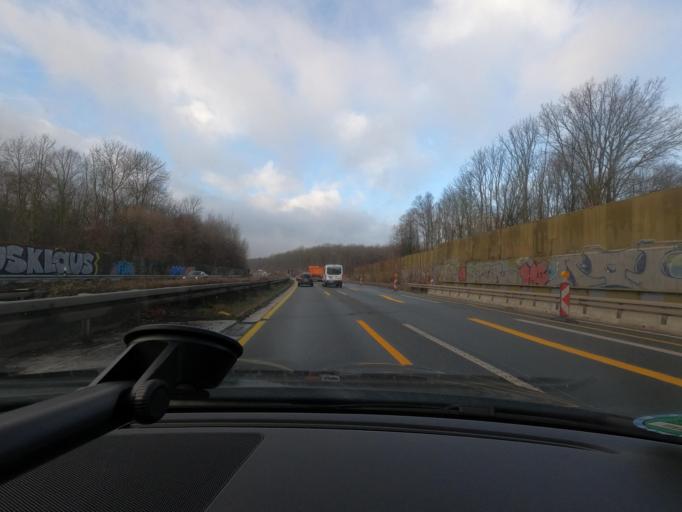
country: DE
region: North Rhine-Westphalia
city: Lanstrop
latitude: 51.5097
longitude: 7.5551
